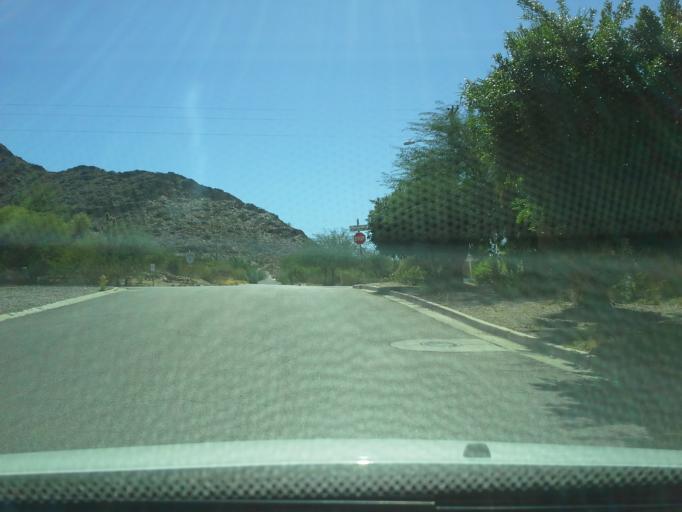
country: US
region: Arizona
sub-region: Maricopa County
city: Paradise Valley
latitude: 33.5717
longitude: -112.0481
